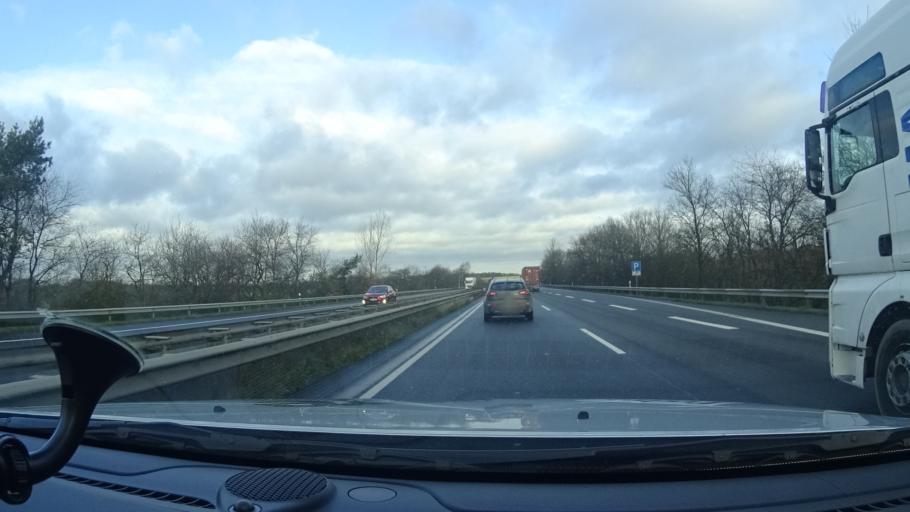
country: DE
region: Lower Saxony
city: Holdorf
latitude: 52.5708
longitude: 8.1107
